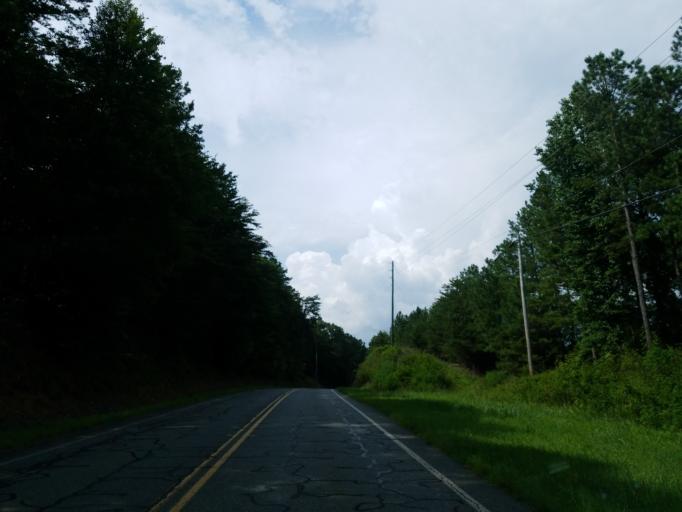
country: US
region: Georgia
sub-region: Gilmer County
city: Ellijay
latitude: 34.6310
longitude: -84.5790
